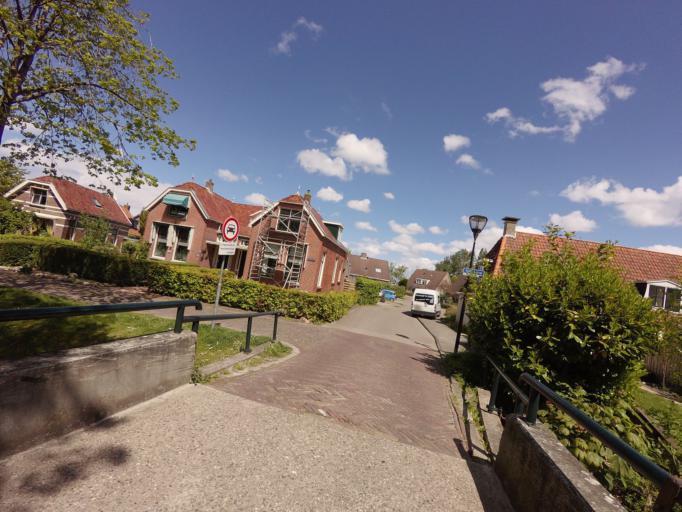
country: NL
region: Friesland
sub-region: Gemeente Franekeradeel
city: Franeker
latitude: 53.1492
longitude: 5.4849
